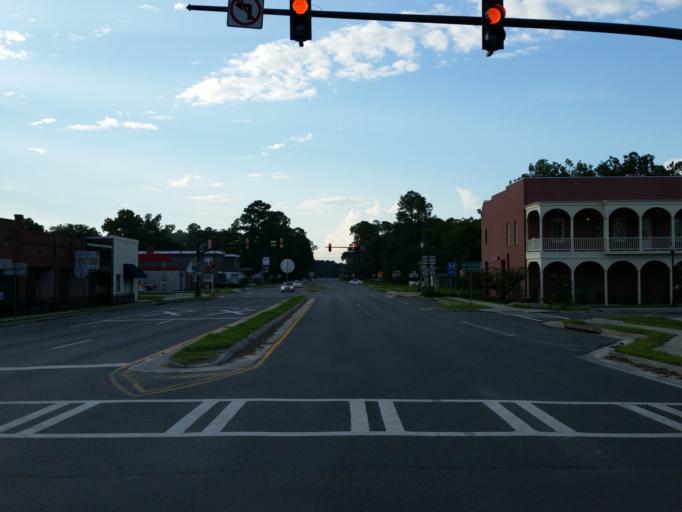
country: US
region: Georgia
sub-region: Clinch County
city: Homerville
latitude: 31.0360
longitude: -82.7468
